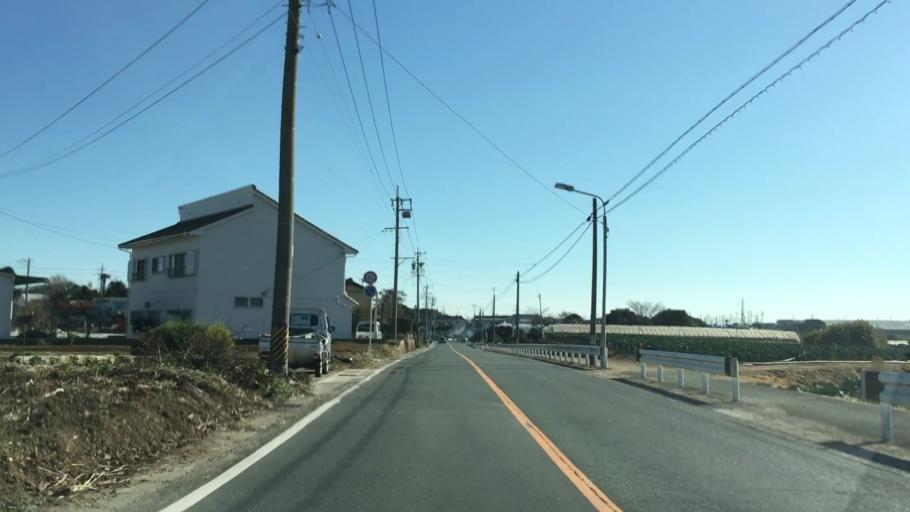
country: JP
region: Aichi
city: Tahara
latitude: 34.6972
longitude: 137.2750
